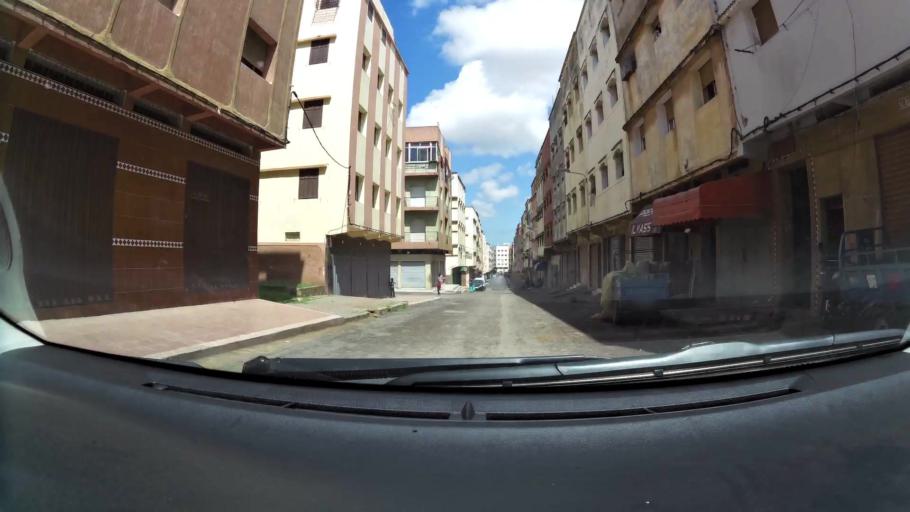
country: MA
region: Grand Casablanca
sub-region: Casablanca
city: Casablanca
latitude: 33.5372
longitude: -7.5668
